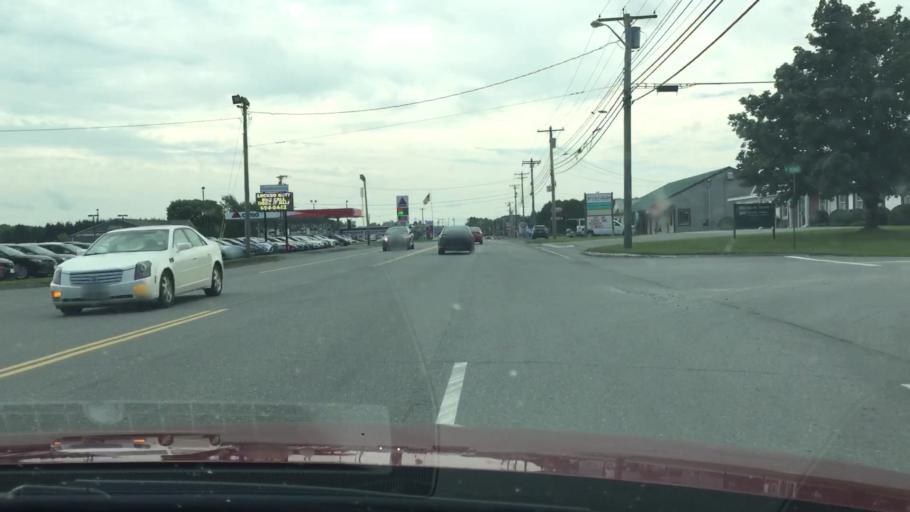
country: US
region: Maine
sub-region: Aroostook County
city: Houlton
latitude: 46.1466
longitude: -67.8405
